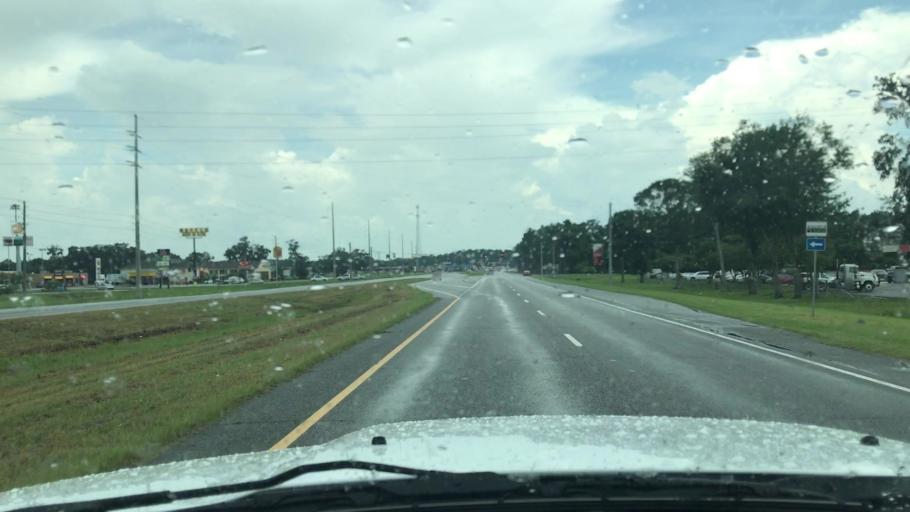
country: US
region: Georgia
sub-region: Glynn County
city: Brunswick
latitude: 31.1391
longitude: -81.5778
